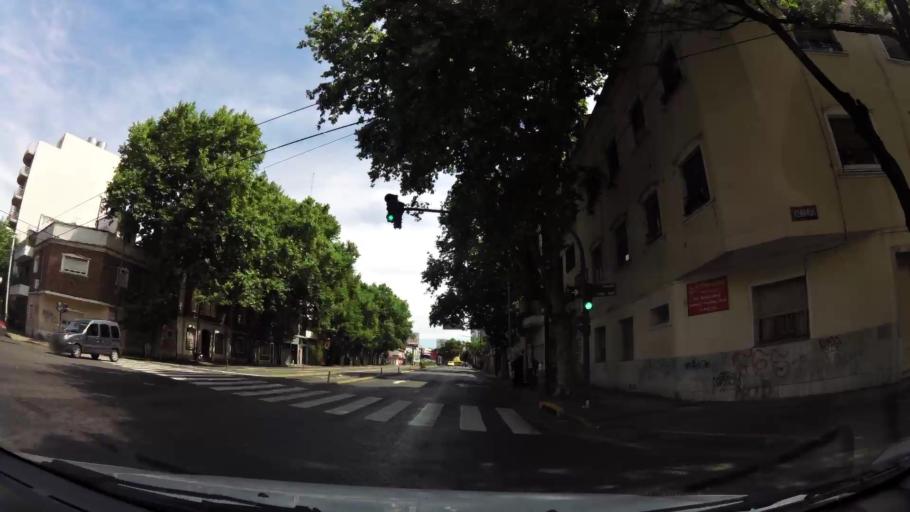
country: AR
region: Buenos Aires F.D.
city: Villa Santa Rita
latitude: -34.6170
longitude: -58.4752
